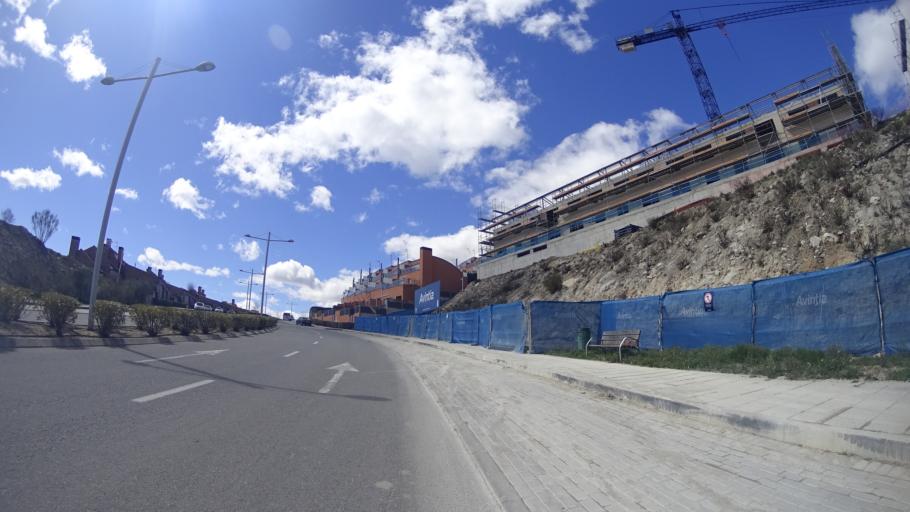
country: ES
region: Madrid
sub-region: Provincia de Madrid
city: Torrelodones
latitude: 40.5656
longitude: -3.9194
